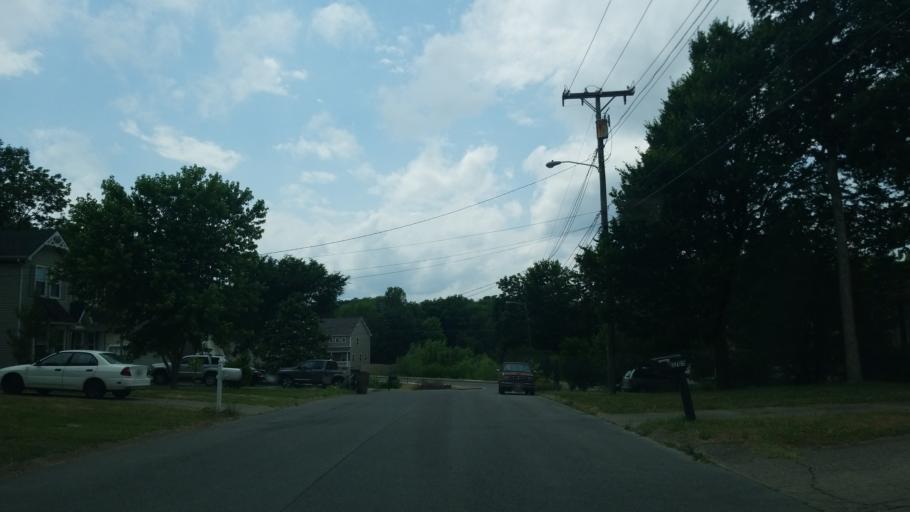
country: US
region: Tennessee
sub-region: Rutherford County
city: La Vergne
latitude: 36.0686
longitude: -86.6120
